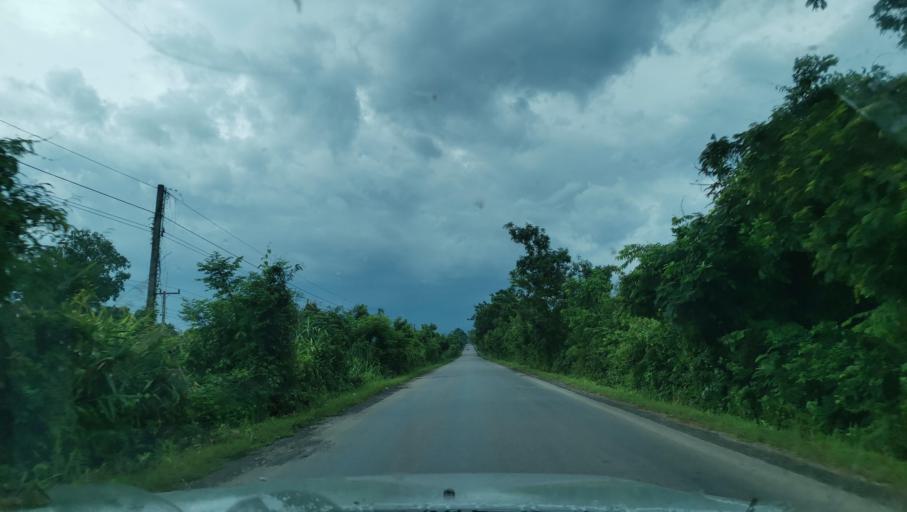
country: TH
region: Nakhon Phanom
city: Ban Phaeng
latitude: 17.8561
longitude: 104.4299
